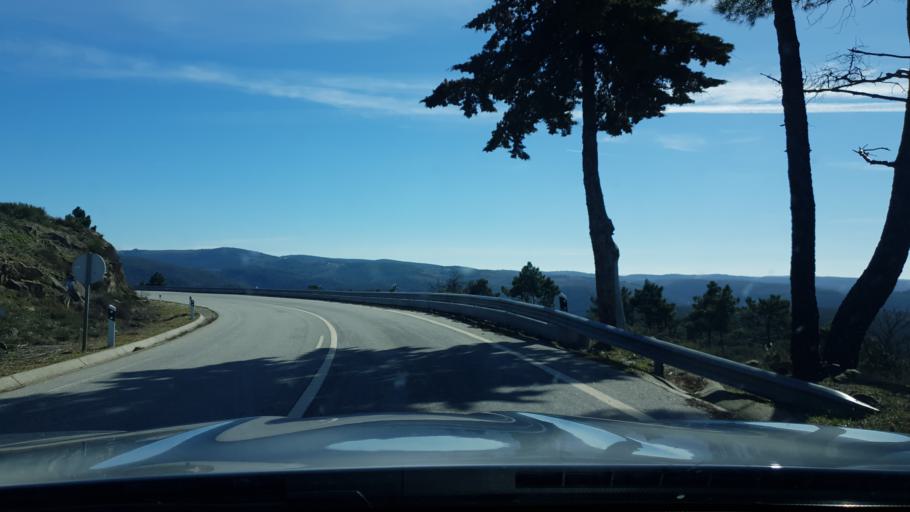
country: PT
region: Braganca
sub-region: Freixo de Espada A Cinta
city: Freixo de Espada a Cinta
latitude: 41.1834
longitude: -6.8661
